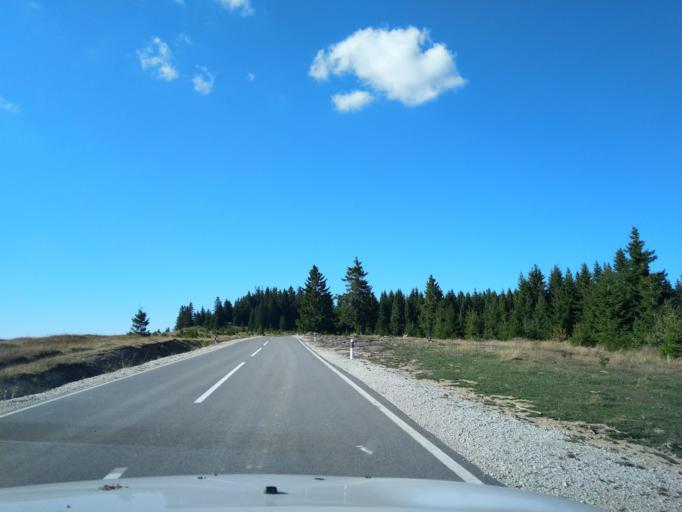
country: RS
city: Sokolovica
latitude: 43.3193
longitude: 20.2908
